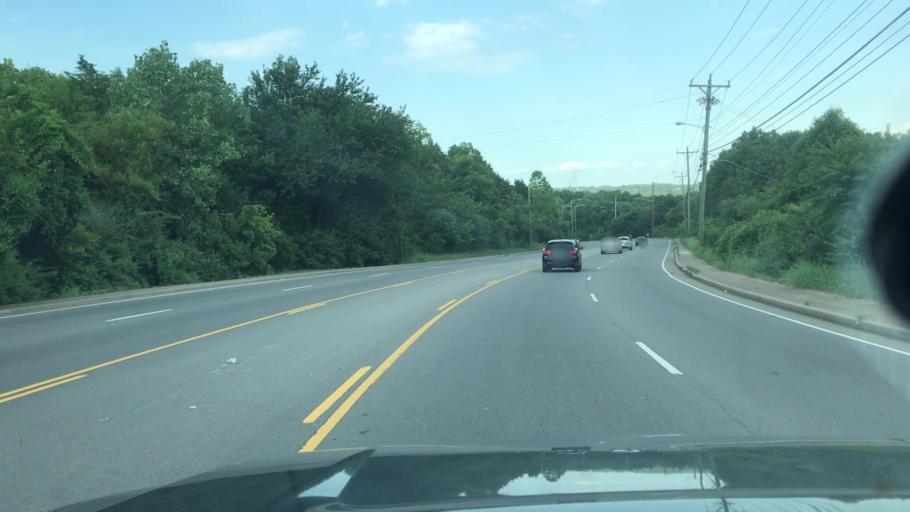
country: US
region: Tennessee
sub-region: Davidson County
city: Nashville
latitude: 36.2007
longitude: -86.8244
